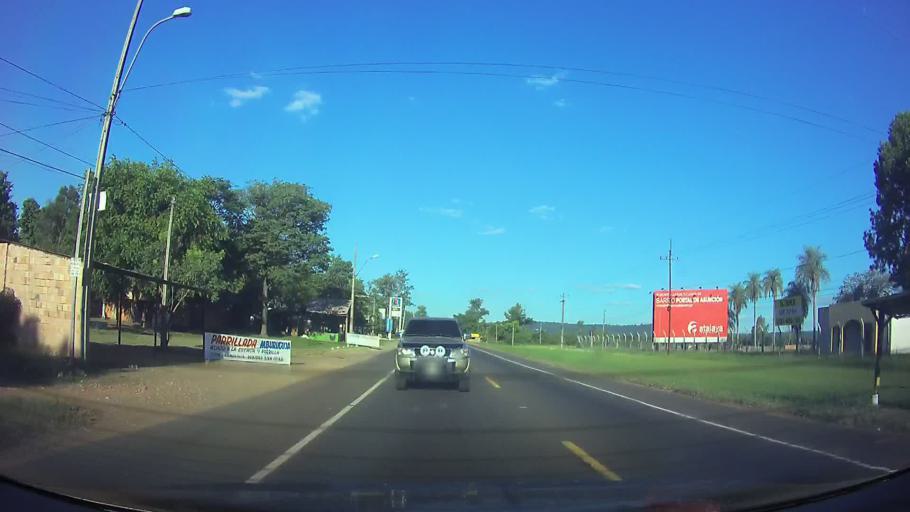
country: PY
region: Central
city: Ypacarai
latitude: -25.3808
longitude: -57.2499
